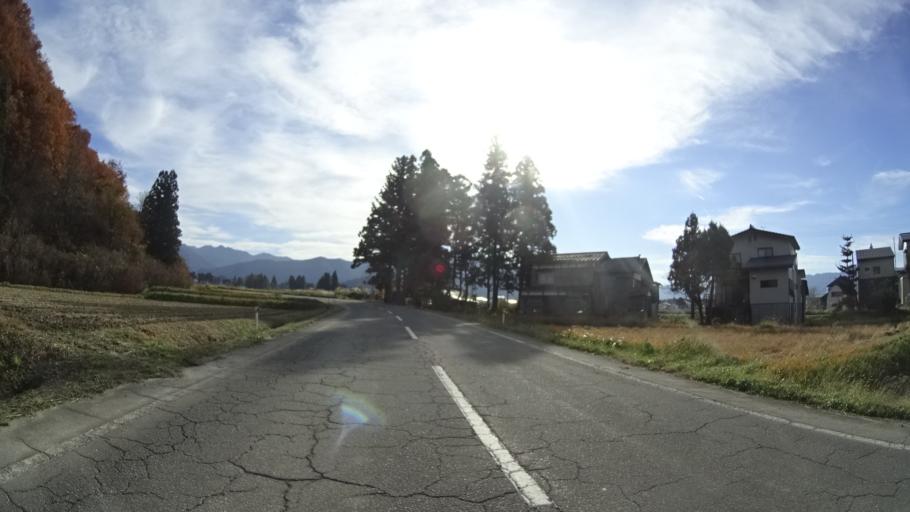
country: JP
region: Niigata
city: Shiozawa
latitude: 37.0242
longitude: 138.8809
